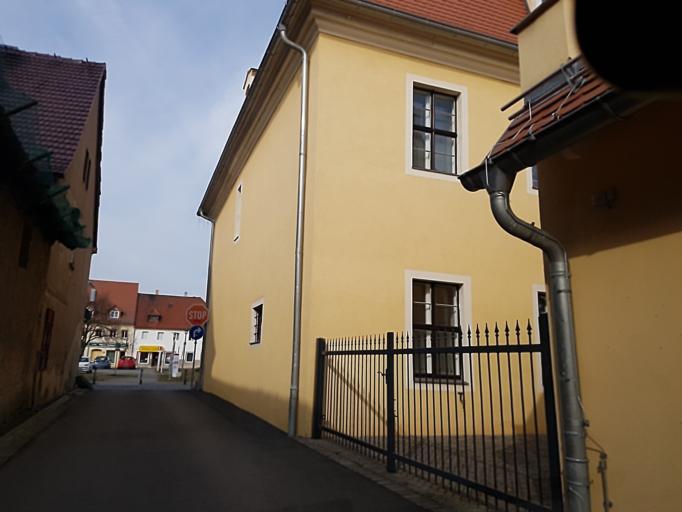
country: DE
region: Brandenburg
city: Doberlug-Kirchhain
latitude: 51.6105
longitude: 13.5500
